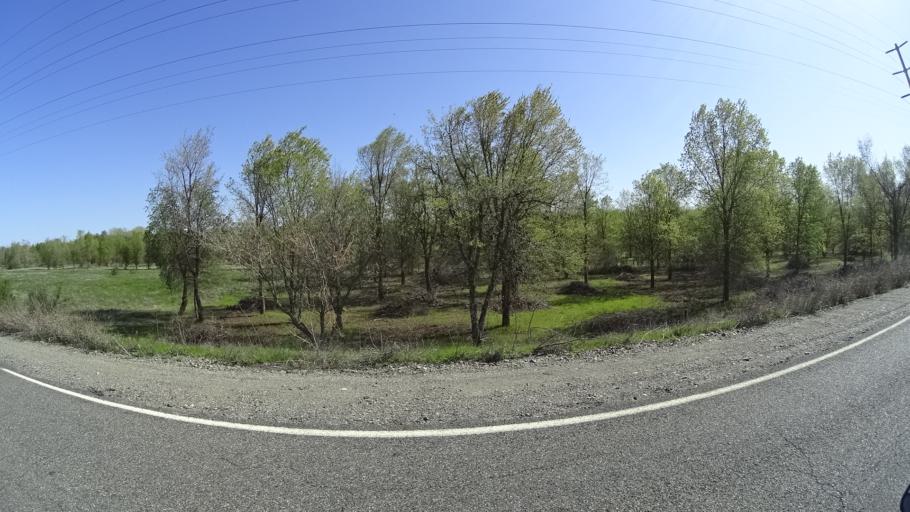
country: US
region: California
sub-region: Glenn County
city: Hamilton City
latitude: 39.7691
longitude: -122.0332
